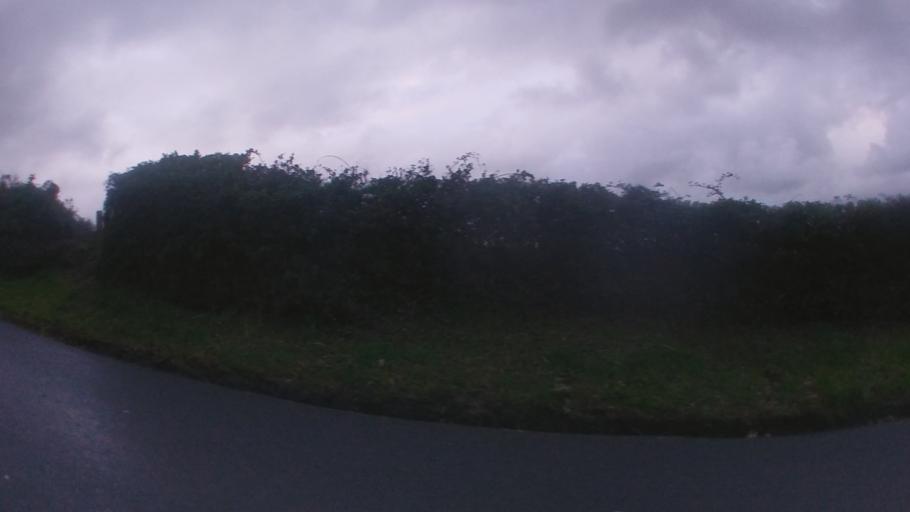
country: IE
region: Leinster
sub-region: Wicklow
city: Kilcoole
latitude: 53.1143
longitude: -6.0613
